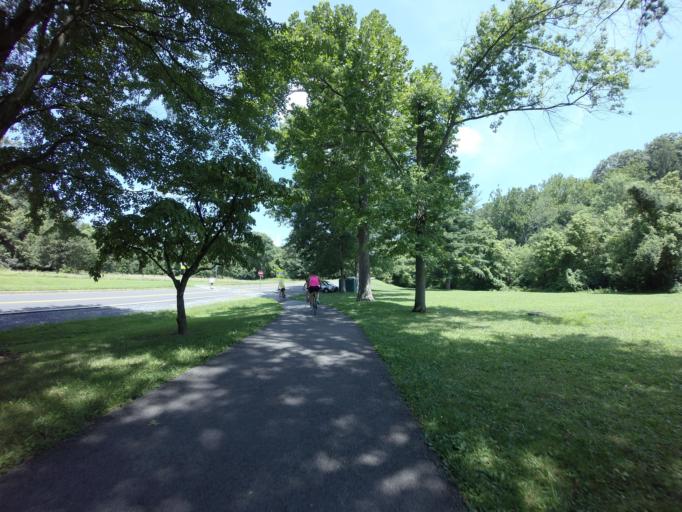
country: US
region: Maryland
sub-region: Montgomery County
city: Forest Glen
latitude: 39.0094
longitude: -77.0631
